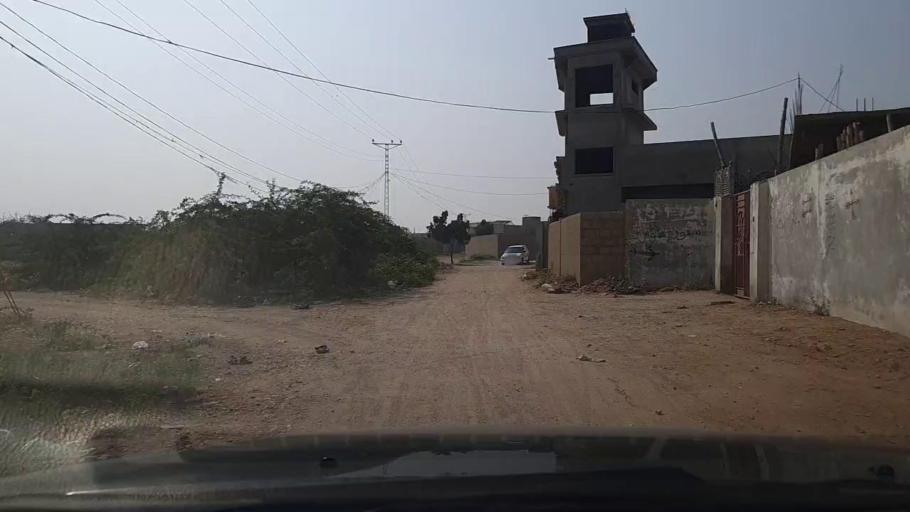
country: PK
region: Sindh
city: Thatta
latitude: 24.7405
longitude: 67.8993
